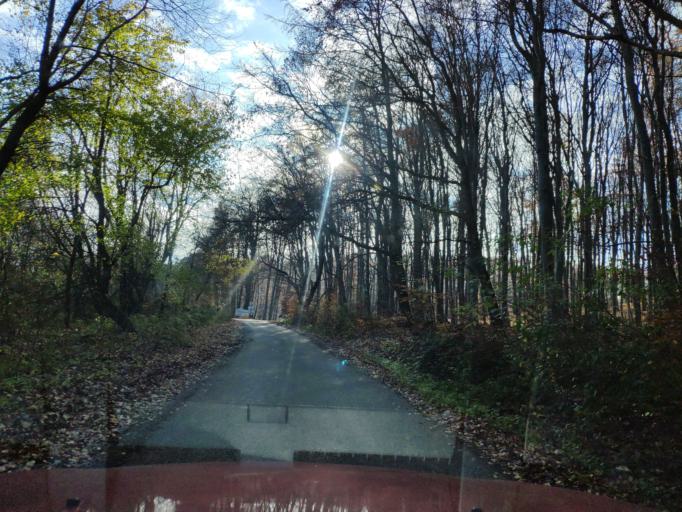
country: SK
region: Kosicky
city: Kosice
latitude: 48.6307
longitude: 21.4528
